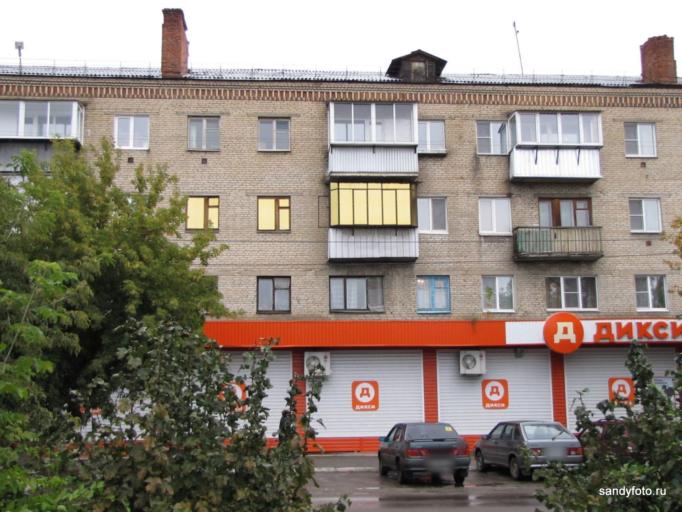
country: RU
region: Chelyabinsk
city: Troitsk
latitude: 54.0880
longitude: 61.5574
